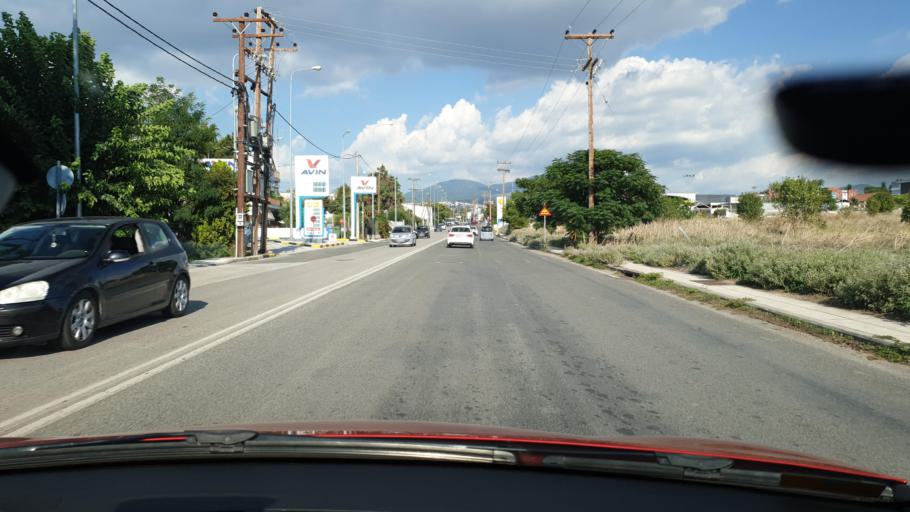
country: GR
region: Central Macedonia
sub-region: Nomos Thessalonikis
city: Kalamaria
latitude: 40.5684
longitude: 22.9776
